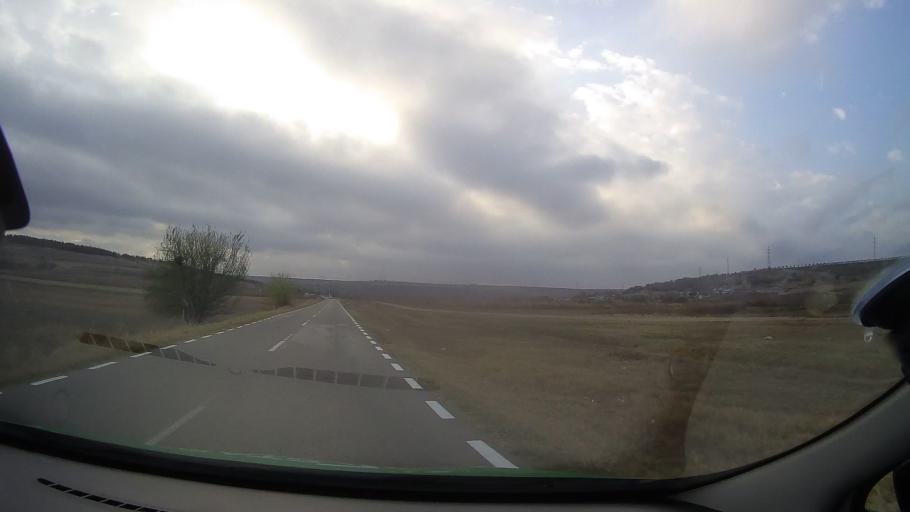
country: RO
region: Constanta
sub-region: Comuna Pestera
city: Pestera
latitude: 44.1981
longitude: 28.1342
